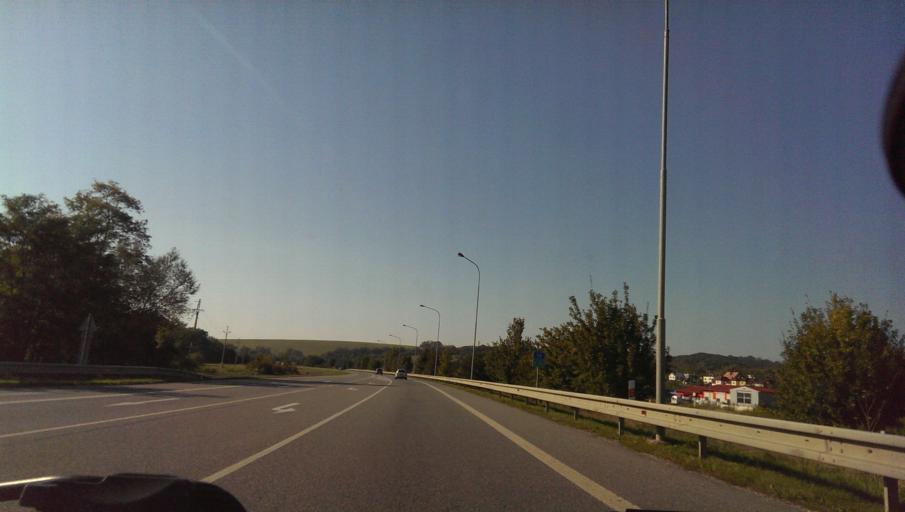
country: CZ
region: Zlin
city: Popovice
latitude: 49.0447
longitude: 17.5272
